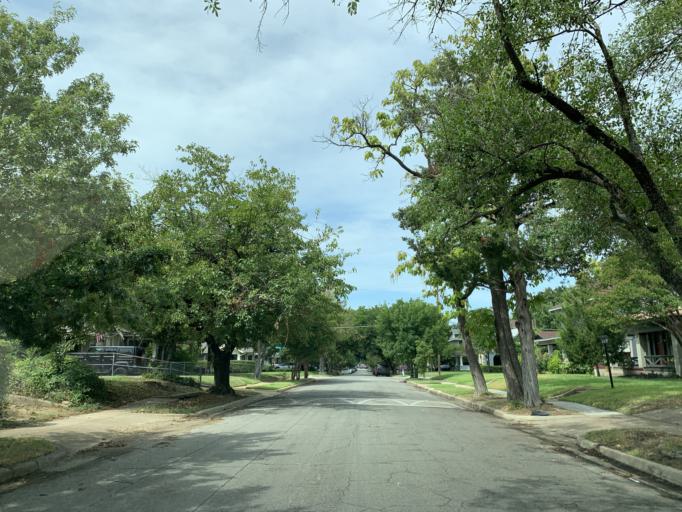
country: US
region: Texas
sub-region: Dallas County
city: Cockrell Hill
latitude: 32.7426
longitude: -96.8479
